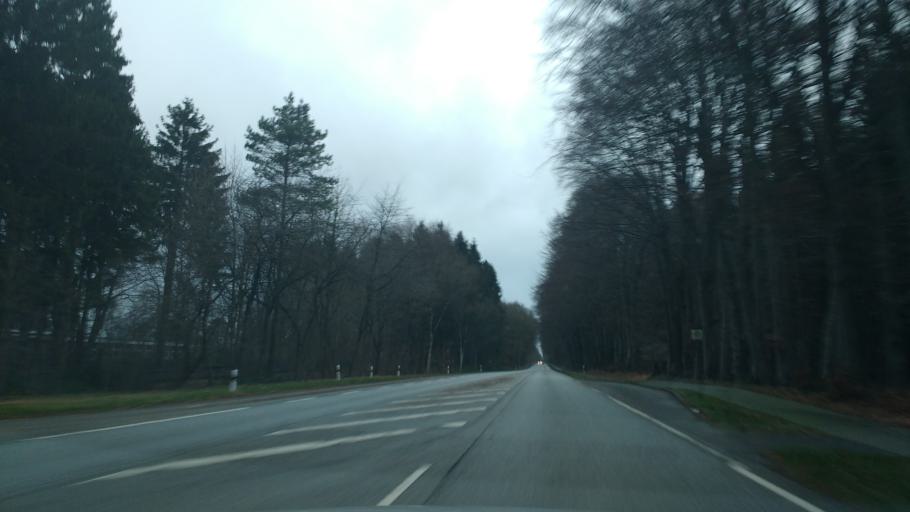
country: DE
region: Schleswig-Holstein
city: Schlotfeld
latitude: 53.9840
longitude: 9.5807
